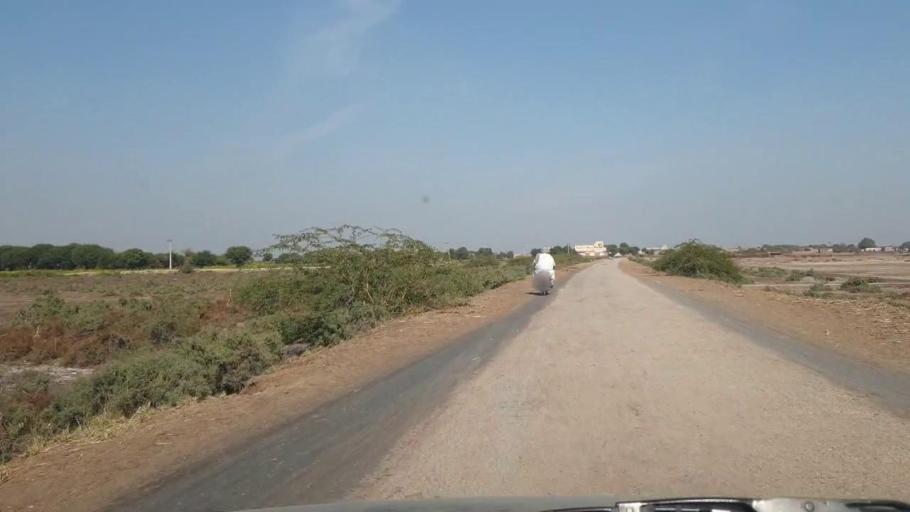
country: PK
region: Sindh
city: Chambar
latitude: 25.3236
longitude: 68.8221
